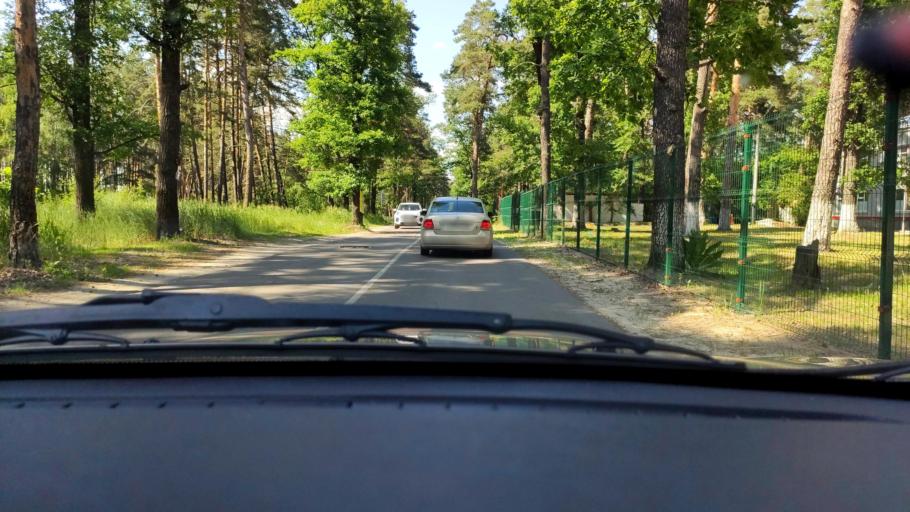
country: RU
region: Voronezj
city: Somovo
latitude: 51.7566
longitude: 39.3661
